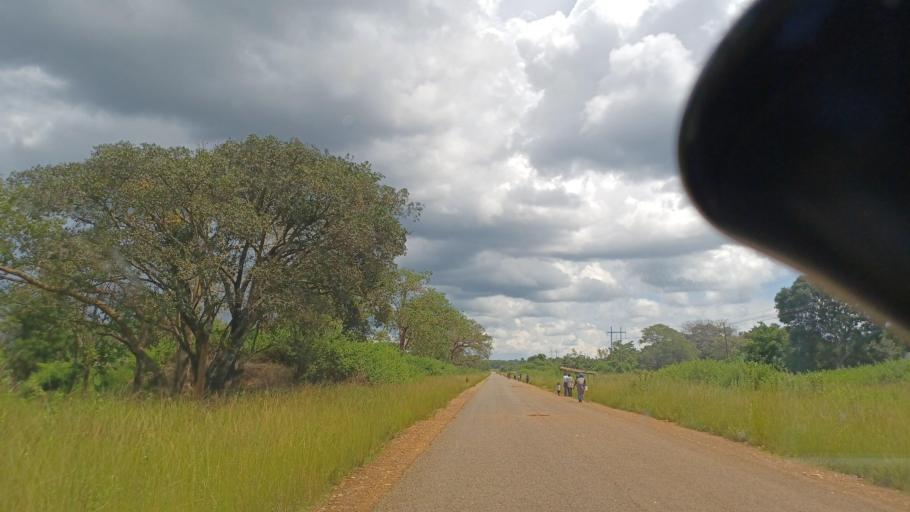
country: ZM
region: North-Western
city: Solwezi
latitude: -12.7708
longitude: 26.0148
